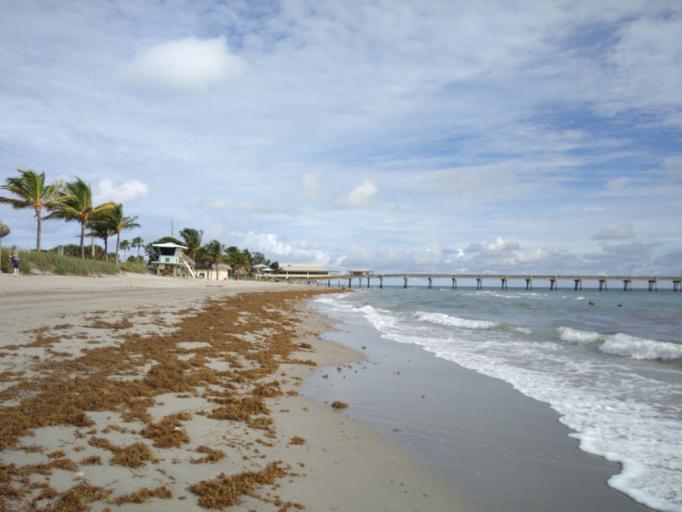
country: US
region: Florida
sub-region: Broward County
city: Dania Beach
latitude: 26.0558
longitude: -80.1117
